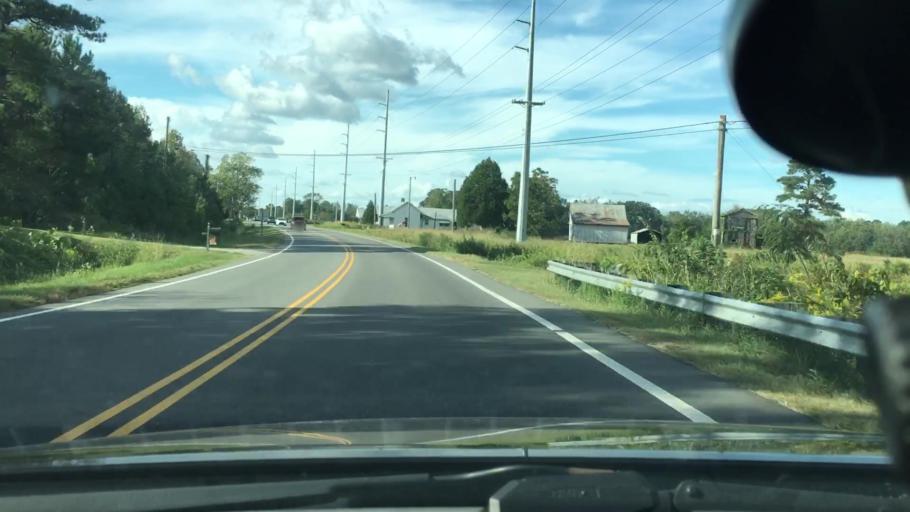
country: US
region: North Carolina
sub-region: Pitt County
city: Windsor
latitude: 35.5494
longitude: -77.3248
